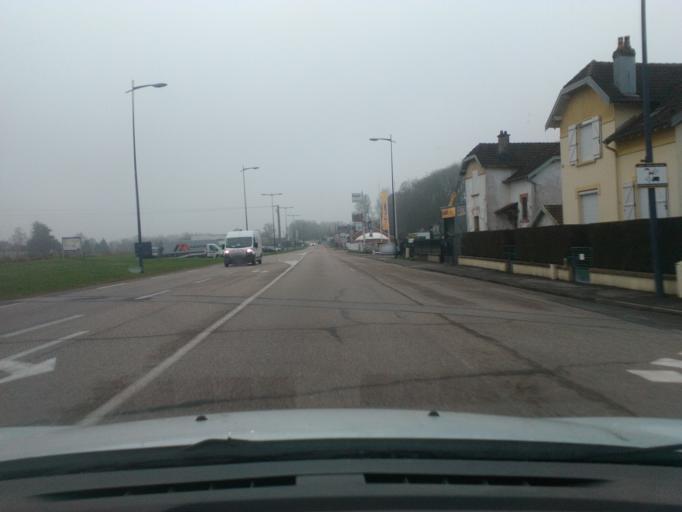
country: FR
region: Lorraine
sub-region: Departement des Vosges
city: Golbey
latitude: 48.2134
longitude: 6.4395
